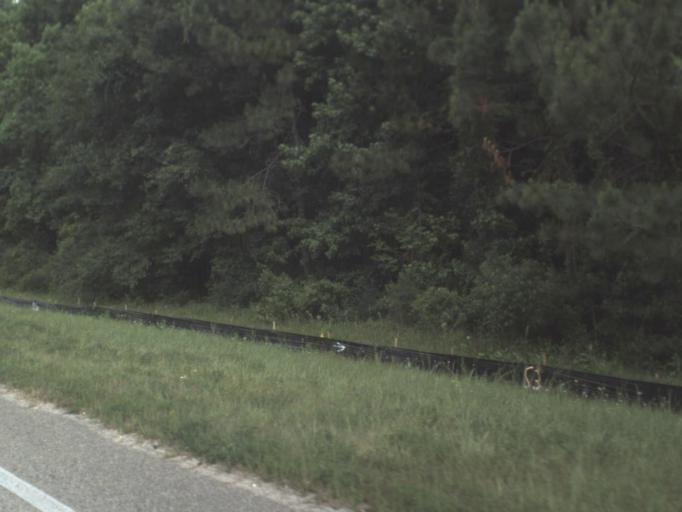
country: US
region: Florida
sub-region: Clay County
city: Middleburg
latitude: 30.0978
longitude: -81.8389
